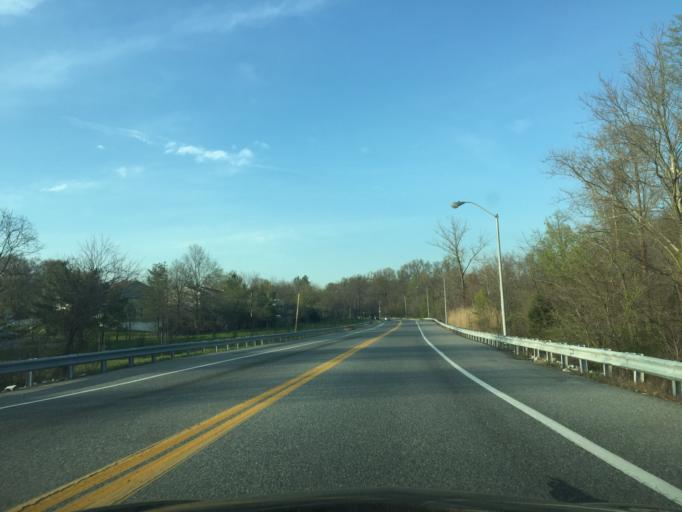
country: US
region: Maryland
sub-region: Baltimore County
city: Perry Hall
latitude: 39.3824
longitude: -76.4709
